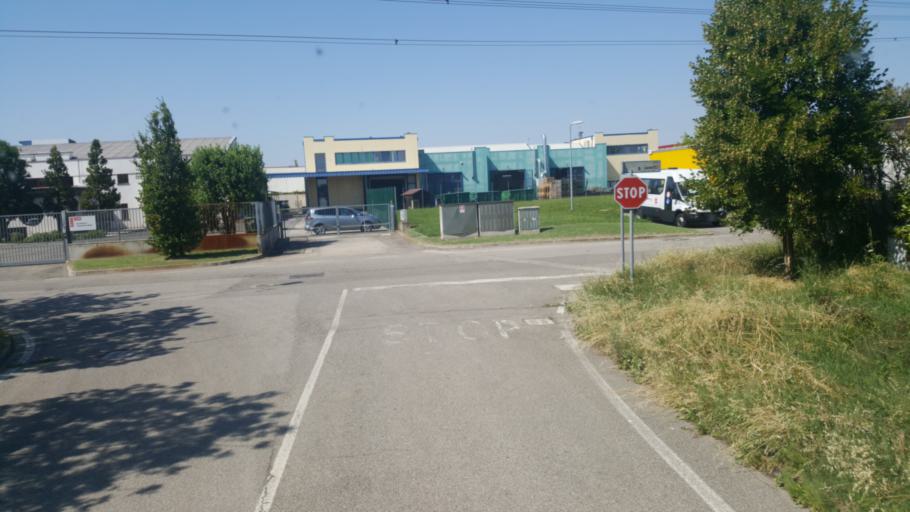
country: IT
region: Emilia-Romagna
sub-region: Provincia di Bologna
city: Castel Maggiore
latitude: 44.6037
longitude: 11.3650
